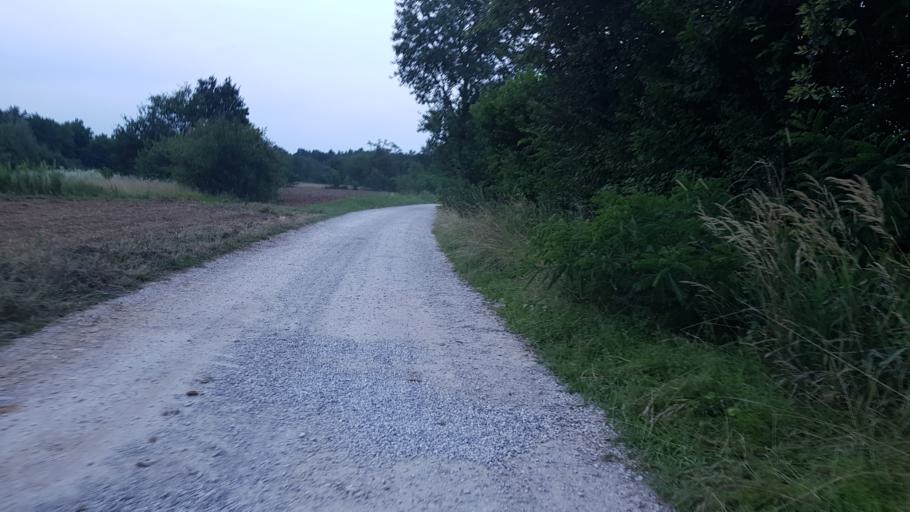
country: IT
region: Friuli Venezia Giulia
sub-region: Provincia di Gorizia
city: San Lorenzo Isontino
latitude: 45.9380
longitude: 13.5277
